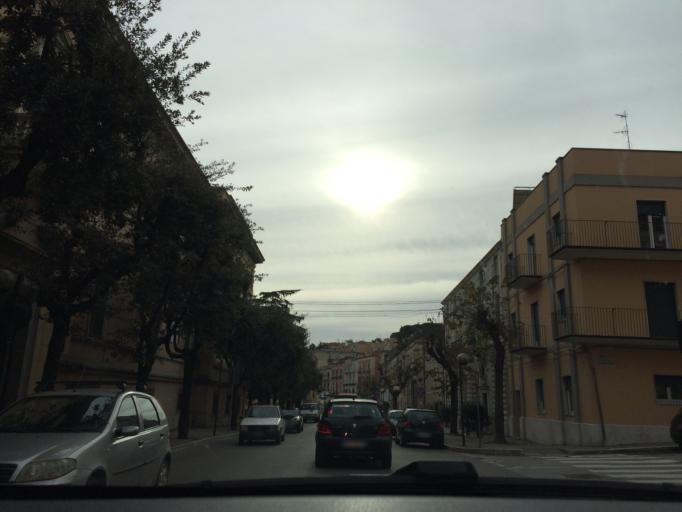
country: IT
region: Basilicate
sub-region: Provincia di Matera
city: Matera
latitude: 40.6624
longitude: 16.6092
